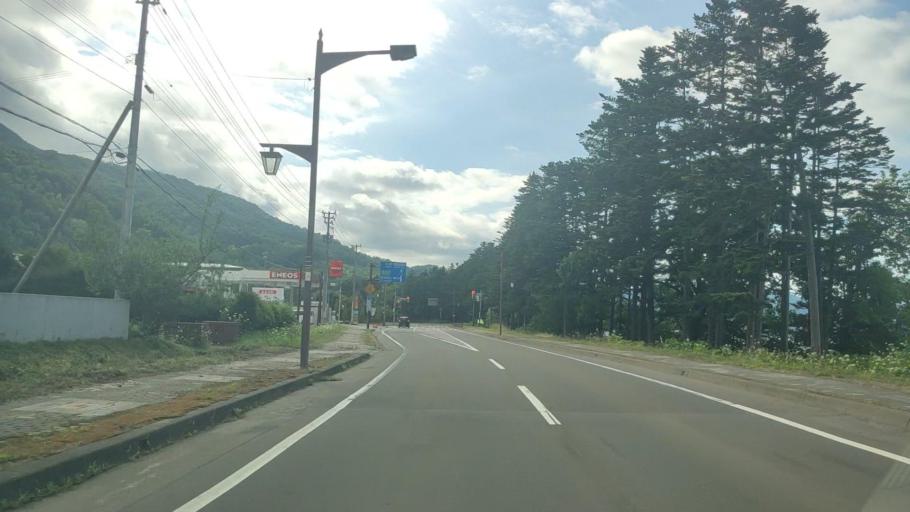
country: JP
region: Hokkaido
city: Date
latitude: 42.5574
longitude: 140.8647
